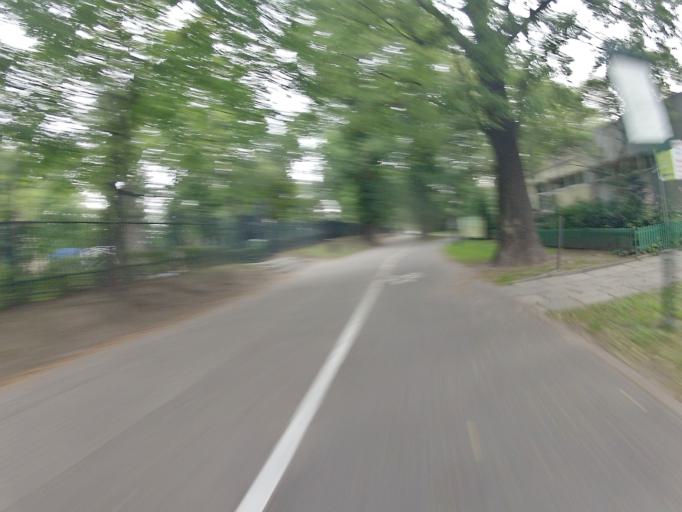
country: PL
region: Lesser Poland Voivodeship
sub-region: Krakow
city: Krakow
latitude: 50.0753
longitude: 19.9107
